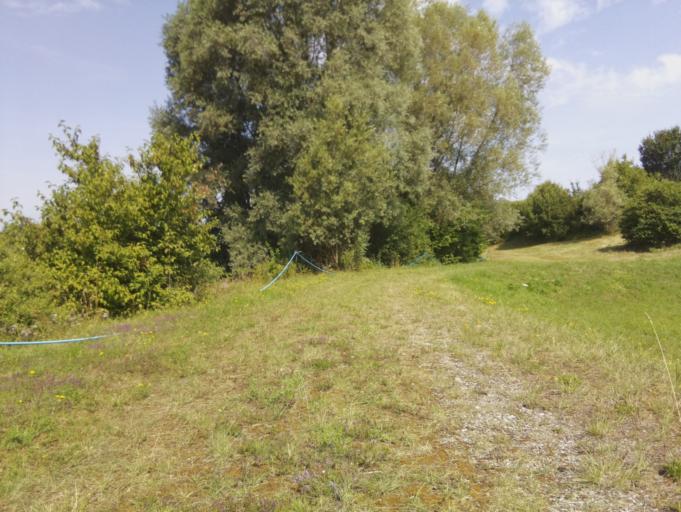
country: CH
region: Zurich
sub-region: Bezirk Andelfingen
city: Henggart
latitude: 47.5768
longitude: 8.6767
